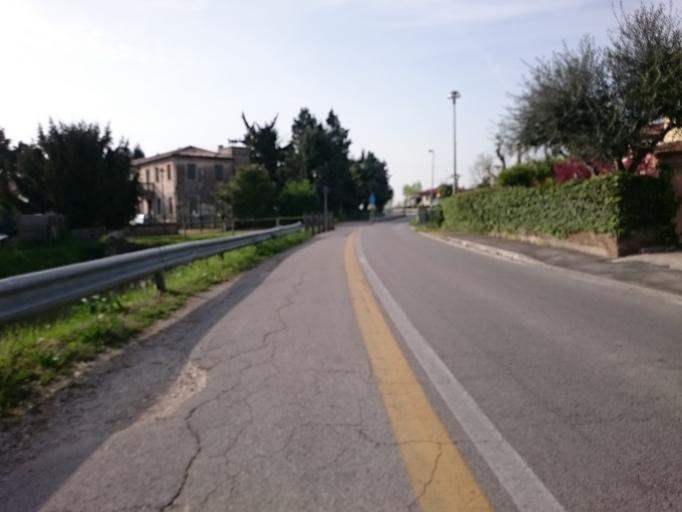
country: IT
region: Veneto
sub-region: Provincia di Padova
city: Bertipaglia
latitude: 45.3157
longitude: 11.8820
